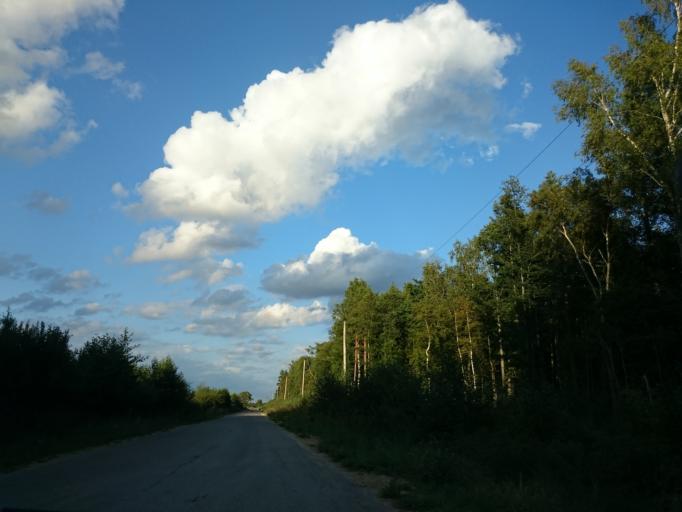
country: LV
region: Adazi
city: Adazi
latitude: 57.0744
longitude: 24.2790
